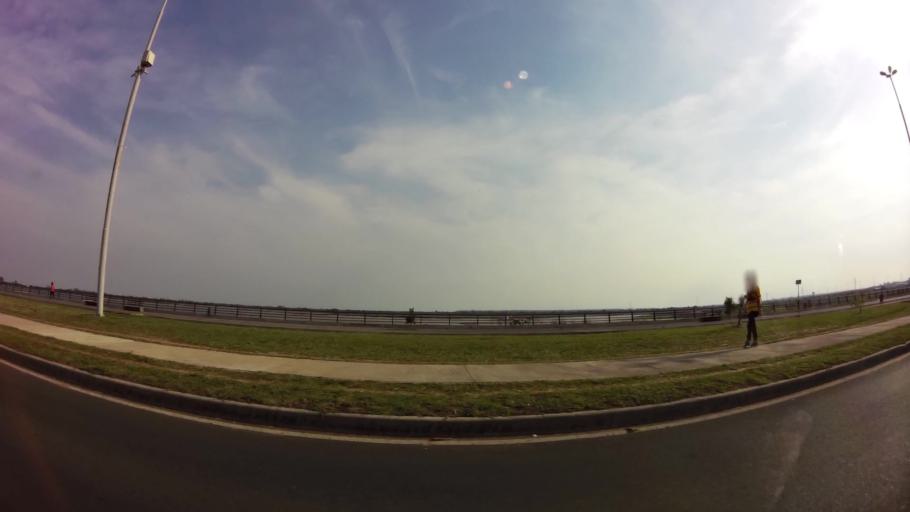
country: PY
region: Asuncion
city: Asuncion
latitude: -25.2767
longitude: -57.6219
